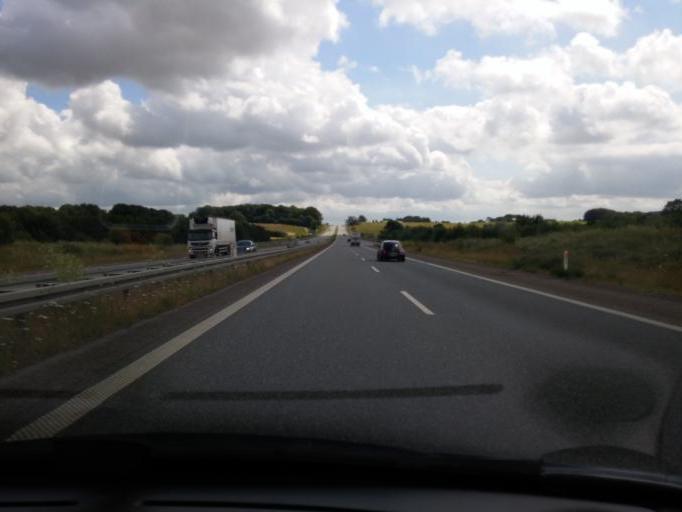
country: DK
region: South Denmark
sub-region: Faaborg-Midtfyn Kommune
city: Ringe
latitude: 55.2357
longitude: 10.4925
